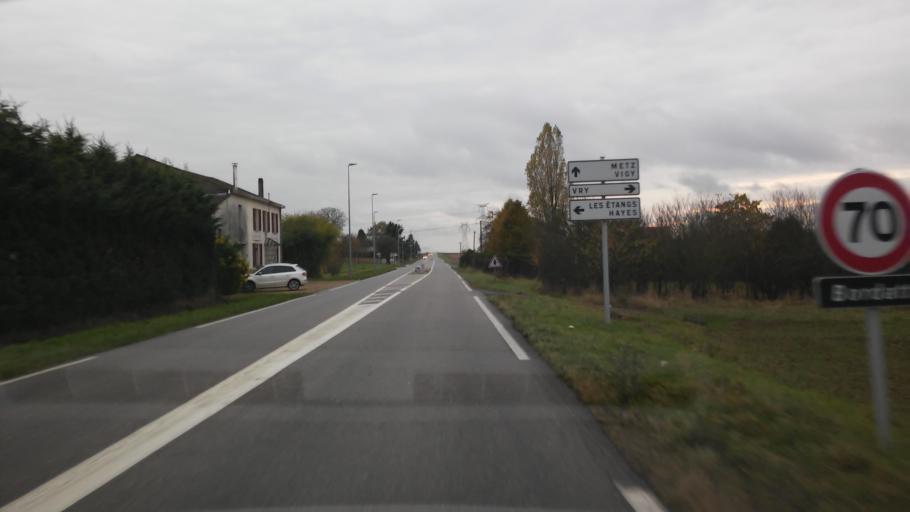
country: FR
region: Lorraine
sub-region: Departement de la Moselle
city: Vigy
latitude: 49.1861
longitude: 6.3349
